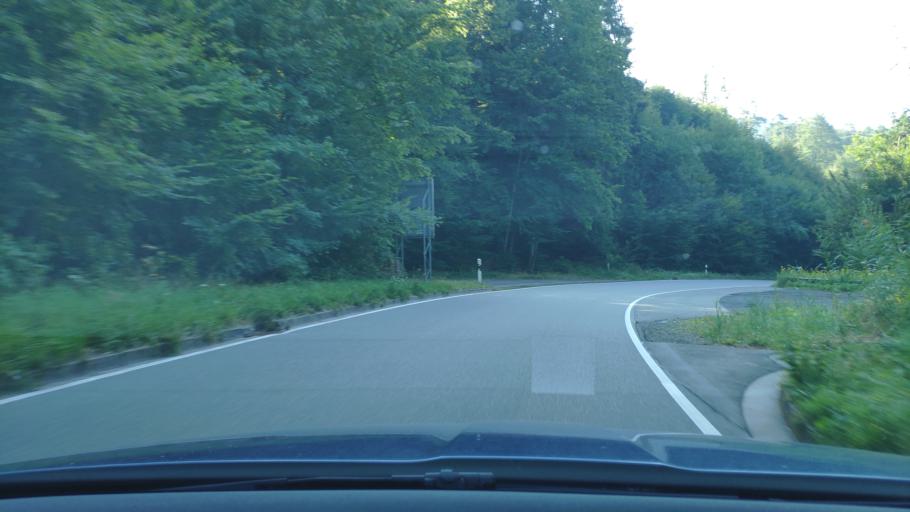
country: DE
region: Rheinland-Pfalz
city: Fischbach
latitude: 49.0659
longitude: 7.7174
